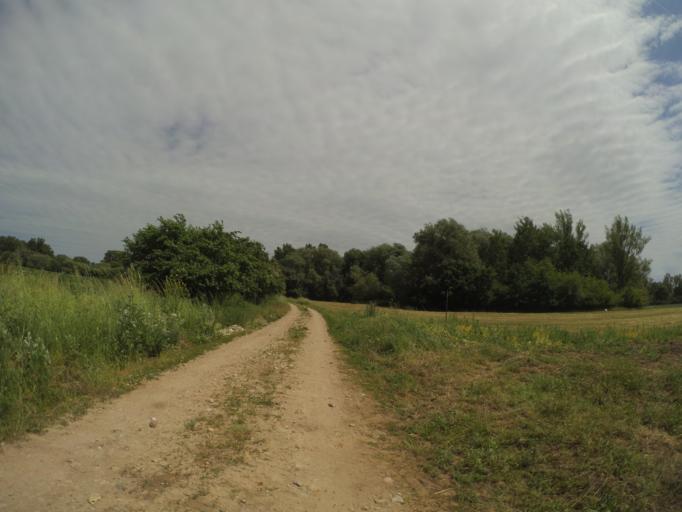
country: CZ
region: Central Bohemia
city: Milovice
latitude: 50.1765
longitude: 14.8916
